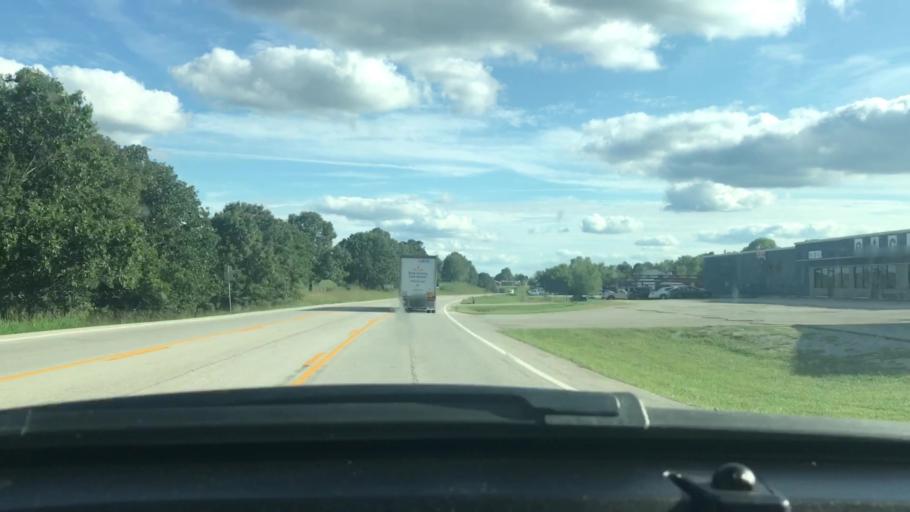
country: US
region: Missouri
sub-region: Oregon County
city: Thayer
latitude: 36.6041
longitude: -91.6443
